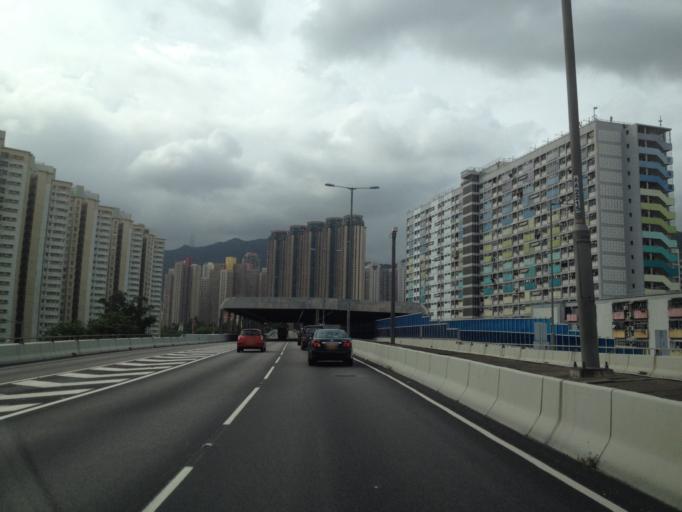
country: HK
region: Wong Tai Sin
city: Wong Tai Sin
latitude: 22.3346
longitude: 114.2050
